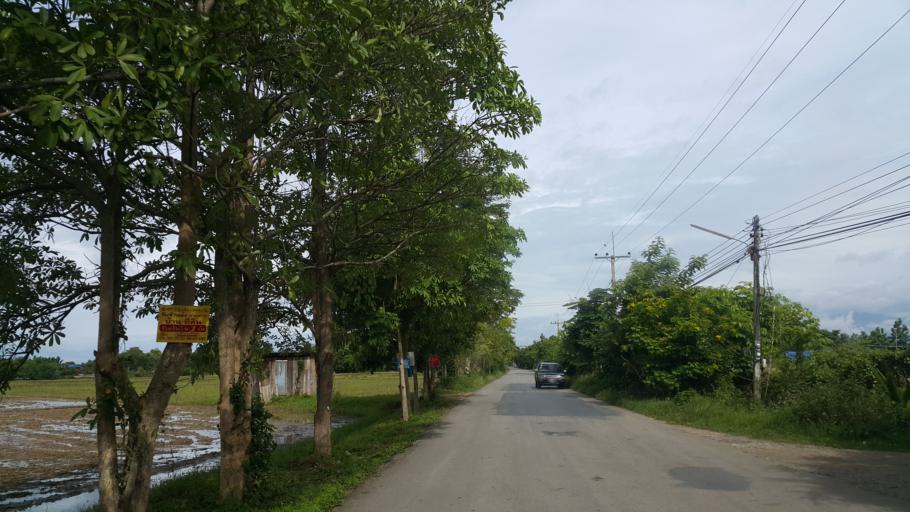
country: TH
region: Chiang Mai
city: San Kamphaeng
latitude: 18.7213
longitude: 99.0923
